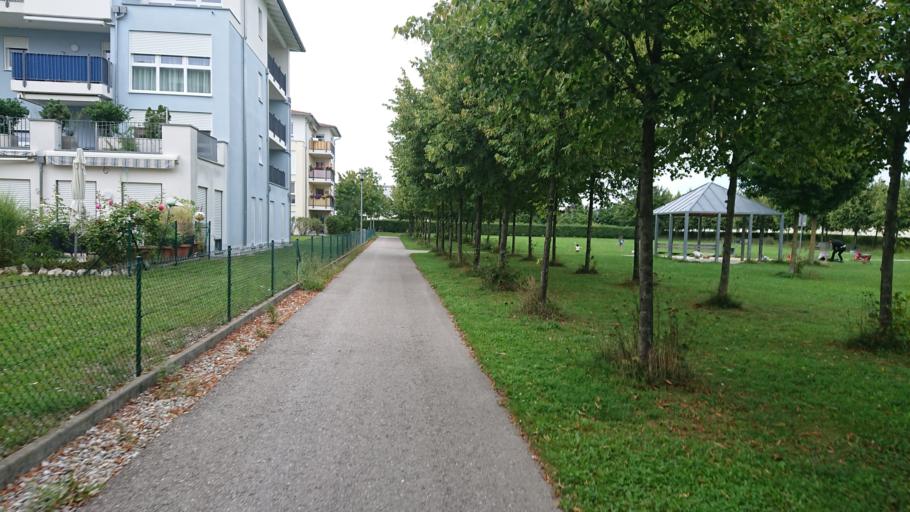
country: DE
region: Bavaria
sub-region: Swabia
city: Stadtbergen
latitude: 48.3660
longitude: 10.8689
